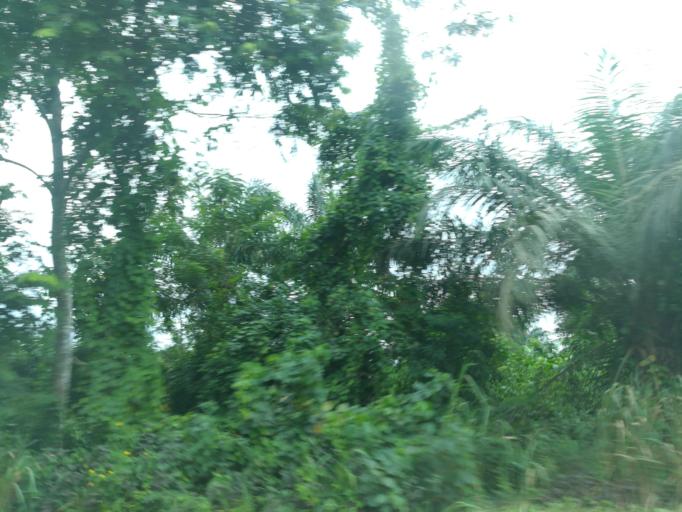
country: NG
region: Lagos
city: Ejirin
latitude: 6.6460
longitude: 3.7768
